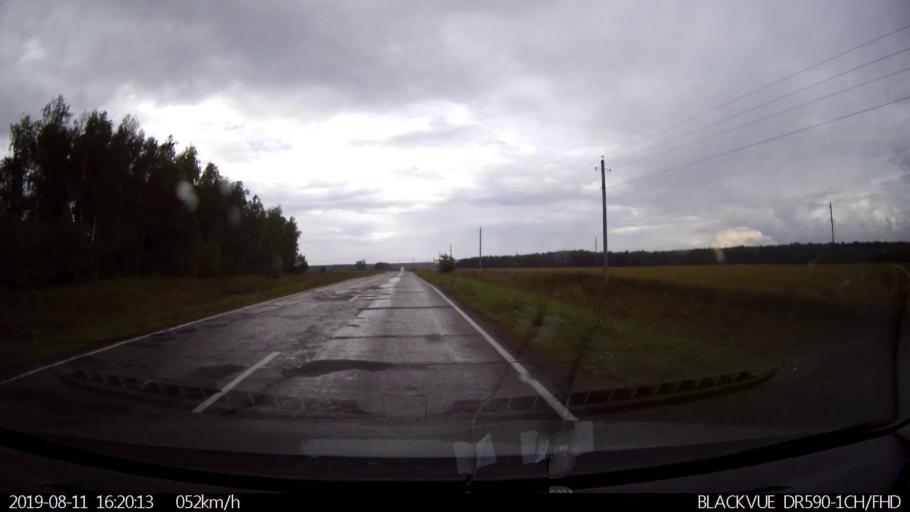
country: RU
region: Ulyanovsk
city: Mayna
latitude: 54.0700
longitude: 47.6040
